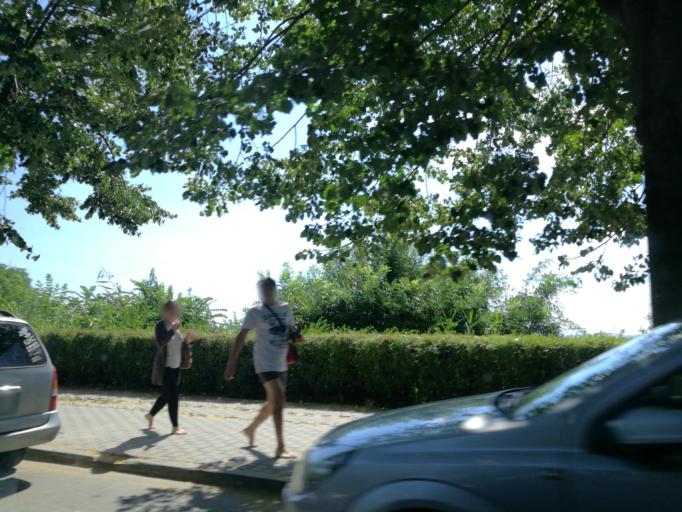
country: RO
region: Constanta
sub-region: Oras Eforie
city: Eforie Nord
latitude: 44.0620
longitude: 28.6376
